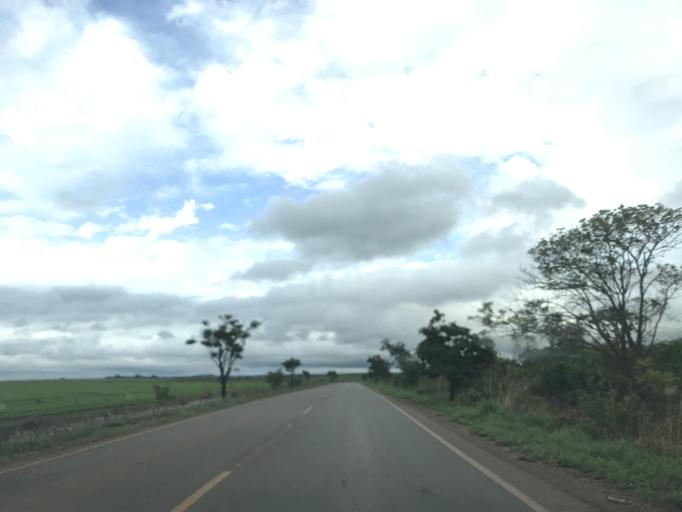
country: BR
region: Goias
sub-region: Vianopolis
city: Vianopolis
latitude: -16.5692
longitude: -48.2919
